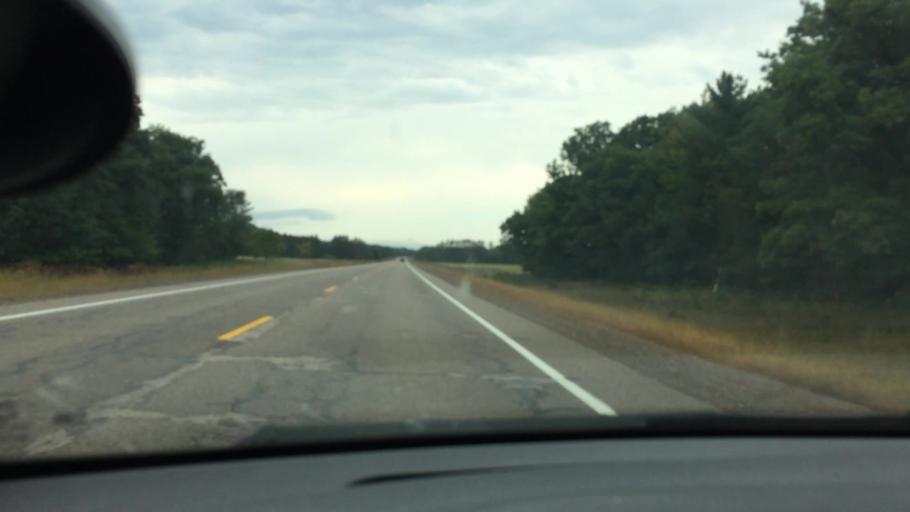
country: US
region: Wisconsin
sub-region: Eau Claire County
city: Augusta
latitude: 44.5800
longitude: -91.0583
